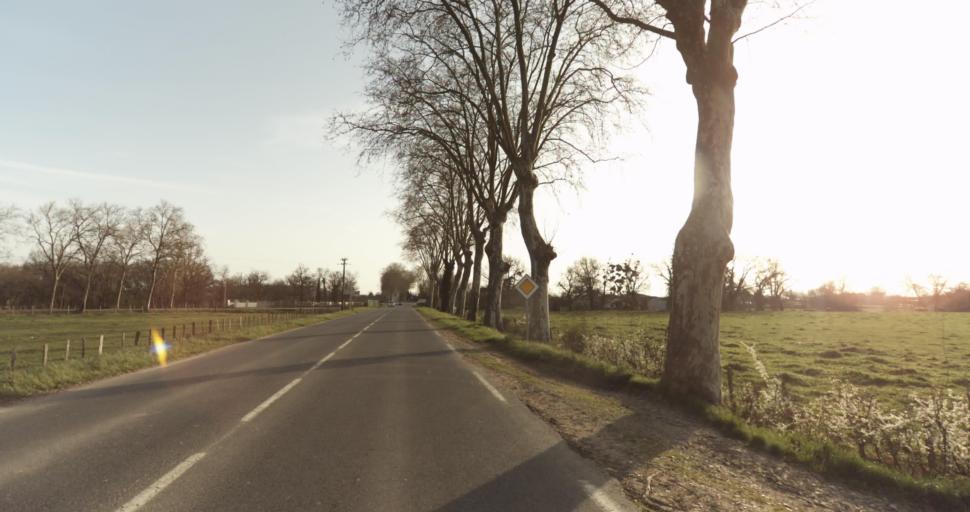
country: FR
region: Midi-Pyrenees
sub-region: Departement du Tarn
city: Saint-Sulpice-la-Pointe
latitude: 43.7732
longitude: 1.6600
